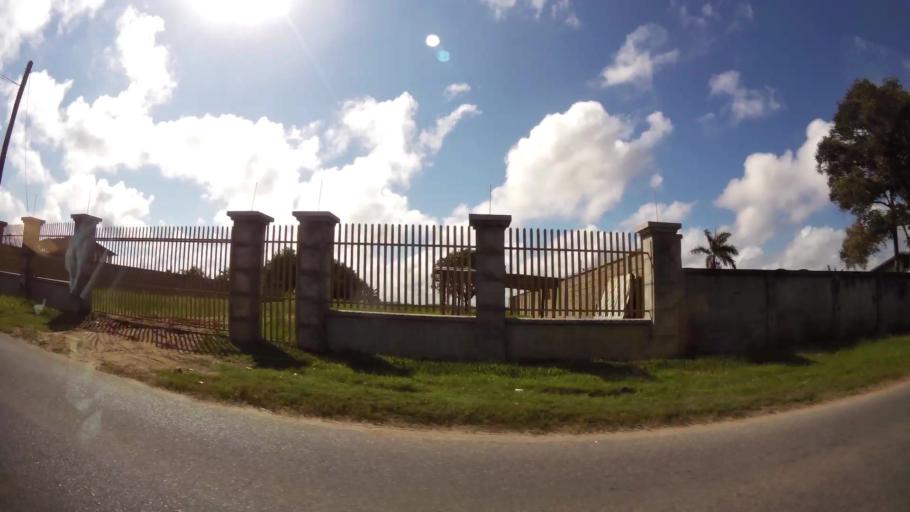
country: SR
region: Commewijne
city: Nieuw Amsterdam
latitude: 5.8558
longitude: -55.1044
